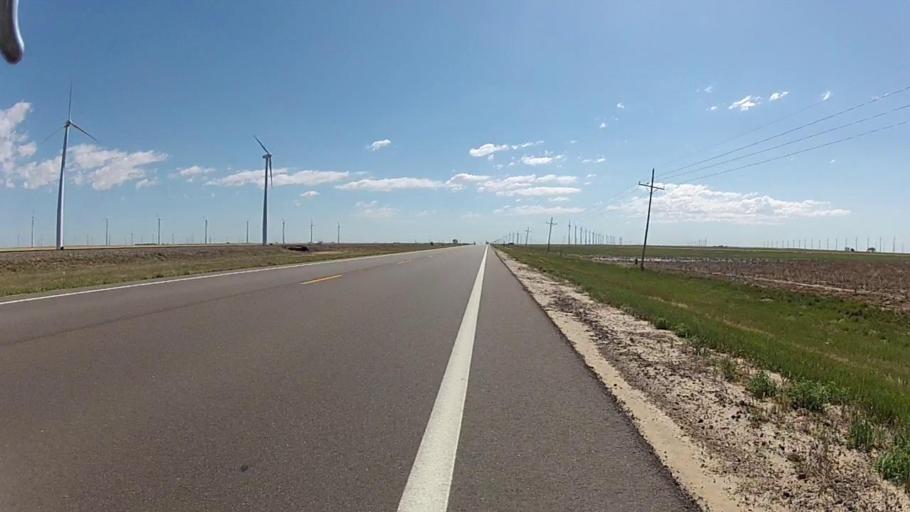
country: US
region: Kansas
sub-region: Gray County
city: Cimarron
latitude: 37.6110
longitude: -100.4011
